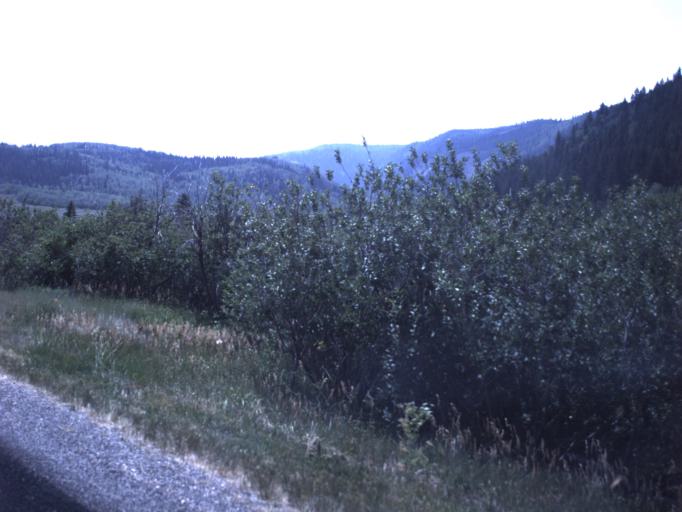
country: US
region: Utah
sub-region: Summit County
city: Francis
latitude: 40.5501
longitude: -111.1022
